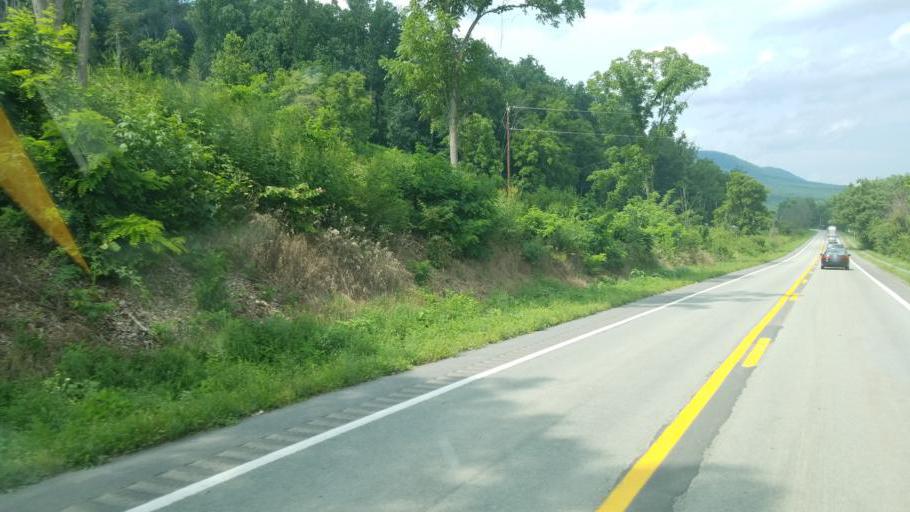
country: US
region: Virginia
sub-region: Frederick County
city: Shawnee Land
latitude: 39.3717
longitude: -78.3715
